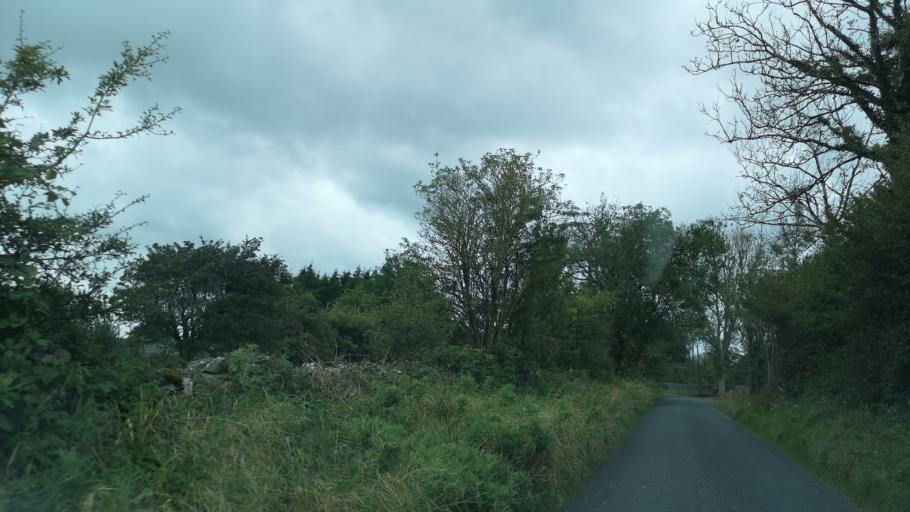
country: IE
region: Connaught
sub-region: County Galway
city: Athenry
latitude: 53.3242
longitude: -8.7403
